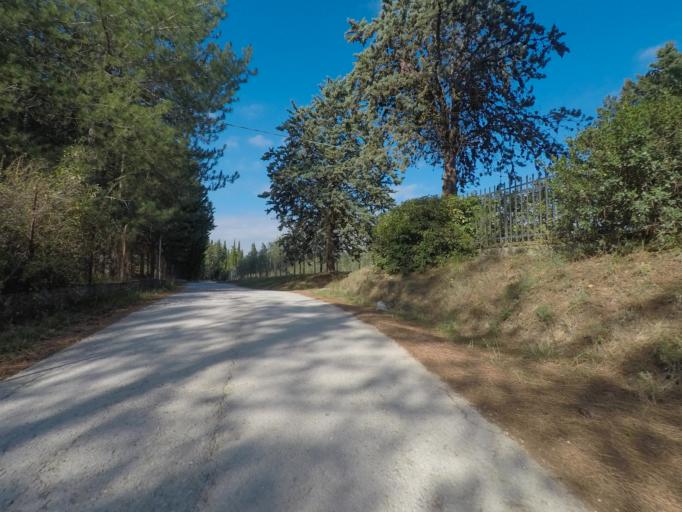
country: IT
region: Tuscany
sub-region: Provincia di Siena
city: Castellina in Chianti
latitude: 43.4404
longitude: 11.3045
